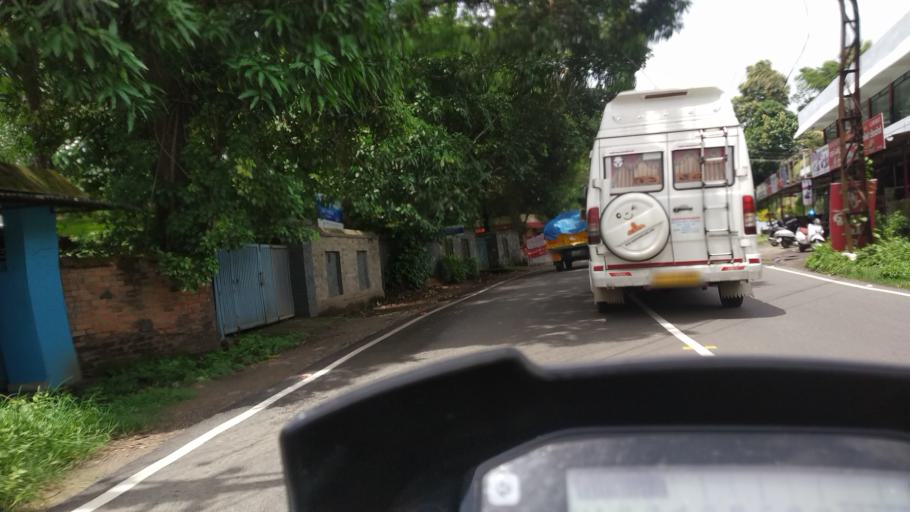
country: IN
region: Kerala
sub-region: Ernakulam
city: Elur
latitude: 10.1360
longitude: 76.2715
